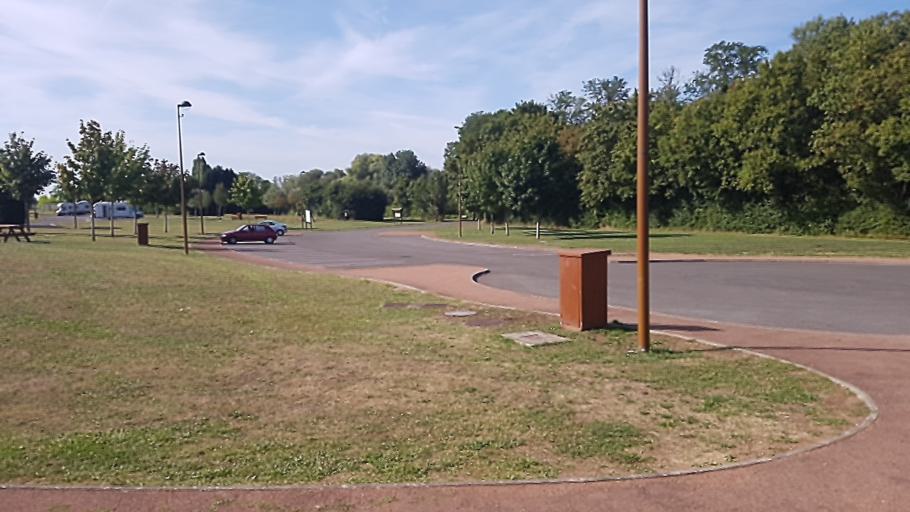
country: FR
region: Bourgogne
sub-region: Departement de la Nievre
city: Imphy
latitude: 46.9234
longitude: 3.2602
